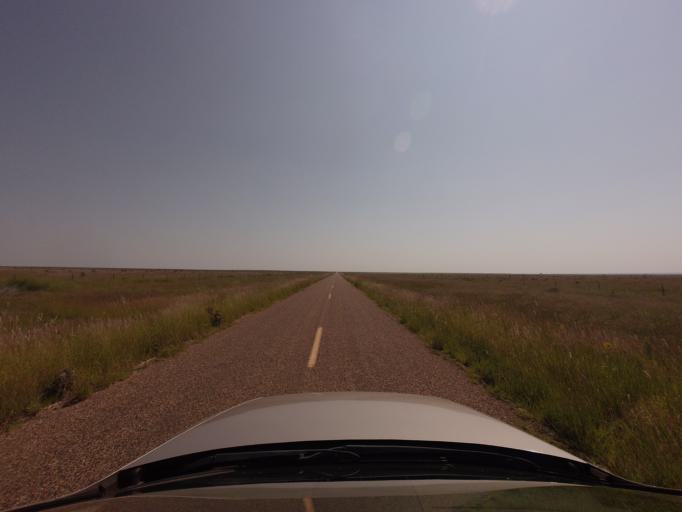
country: US
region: New Mexico
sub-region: Curry County
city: Cannon Air Force Base
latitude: 34.6332
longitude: -103.4238
